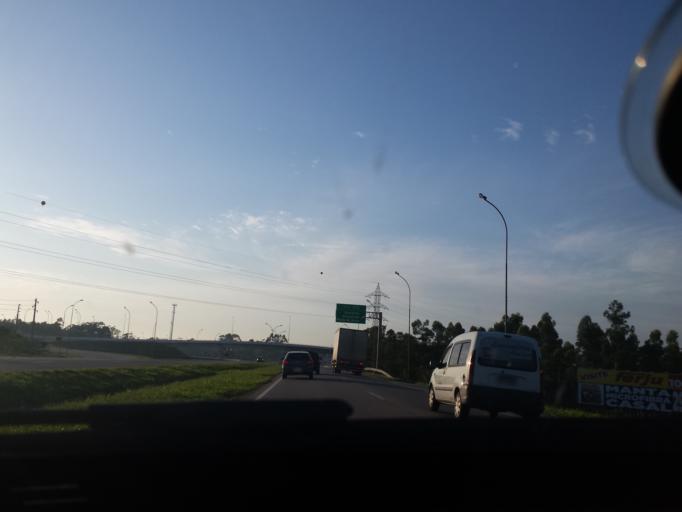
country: BR
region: Santa Catarina
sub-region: Imbituba
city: Imbituba
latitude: -28.1276
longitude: -48.6943
